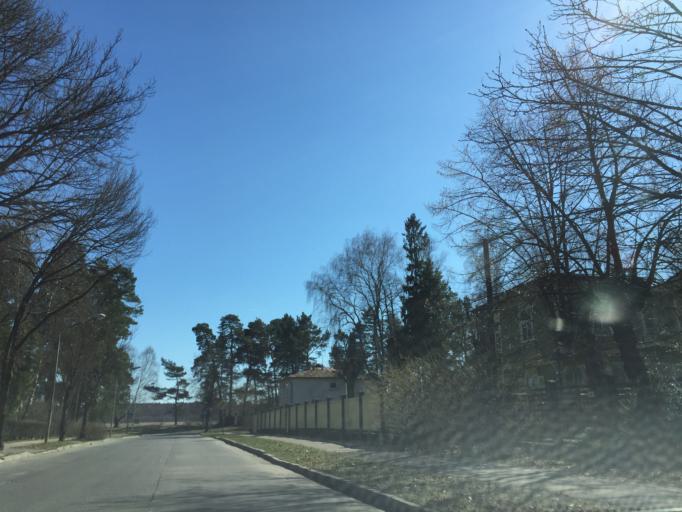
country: LV
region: Babite
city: Pinki
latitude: 56.9833
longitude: 23.8796
